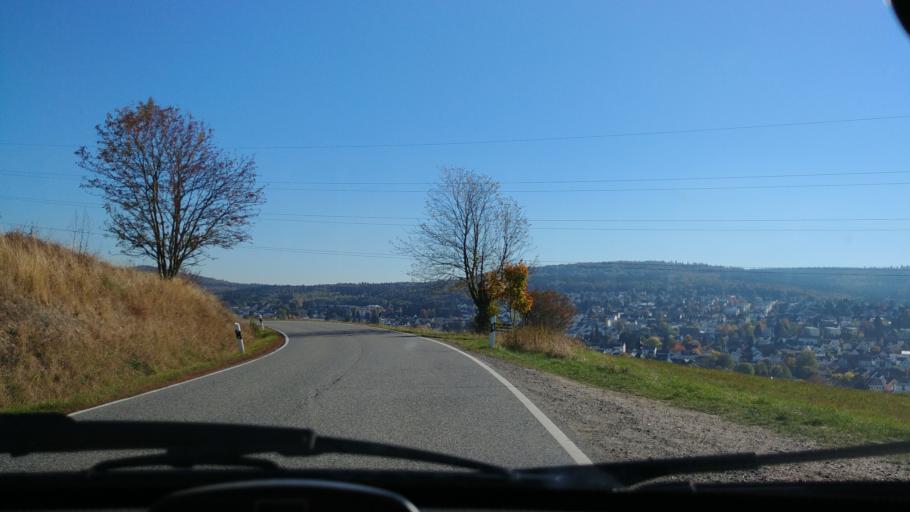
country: DE
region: Hesse
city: Taunusstein
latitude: 50.1440
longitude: 8.1333
